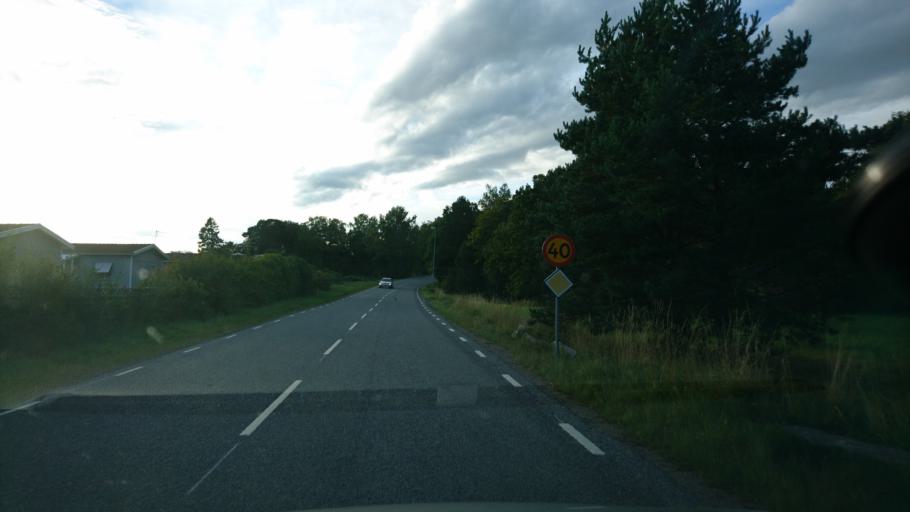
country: SE
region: Soedermanland
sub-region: Strangnas Kommun
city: Stallarholmen
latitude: 59.3689
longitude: 17.2006
